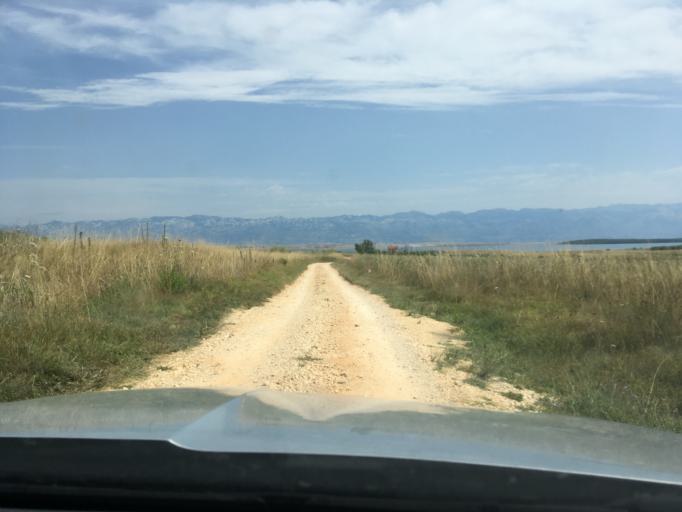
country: HR
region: Zadarska
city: Privlaka
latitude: 44.2631
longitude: 15.1464
